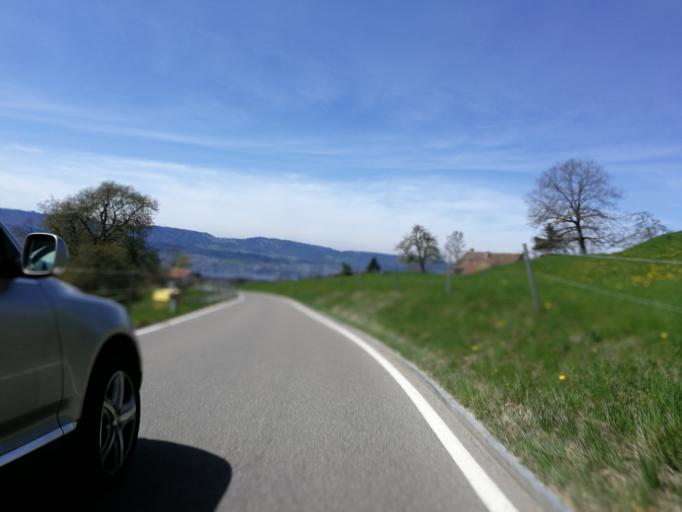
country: CH
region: Zurich
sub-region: Bezirk Meilen
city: Obermeilen
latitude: 47.2863
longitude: 8.6594
